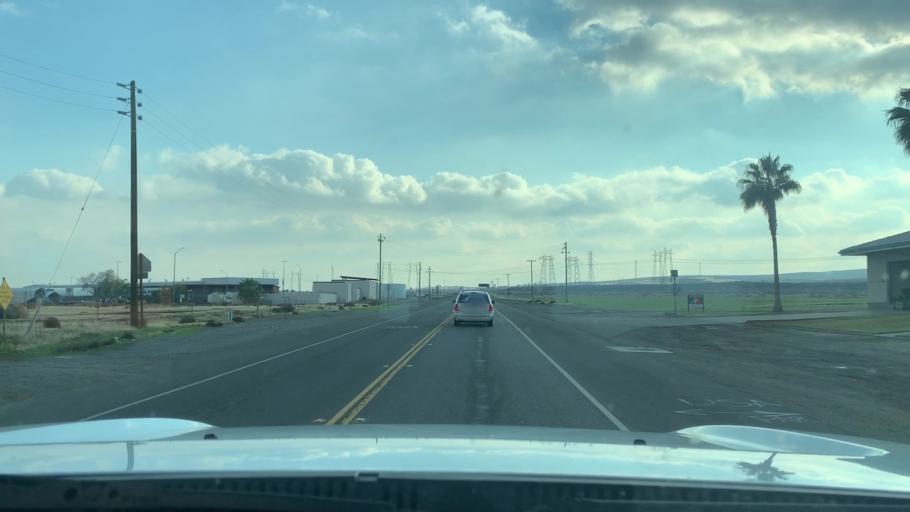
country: US
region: California
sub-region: Kings County
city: Kettleman City
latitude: 36.0073
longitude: -119.9594
